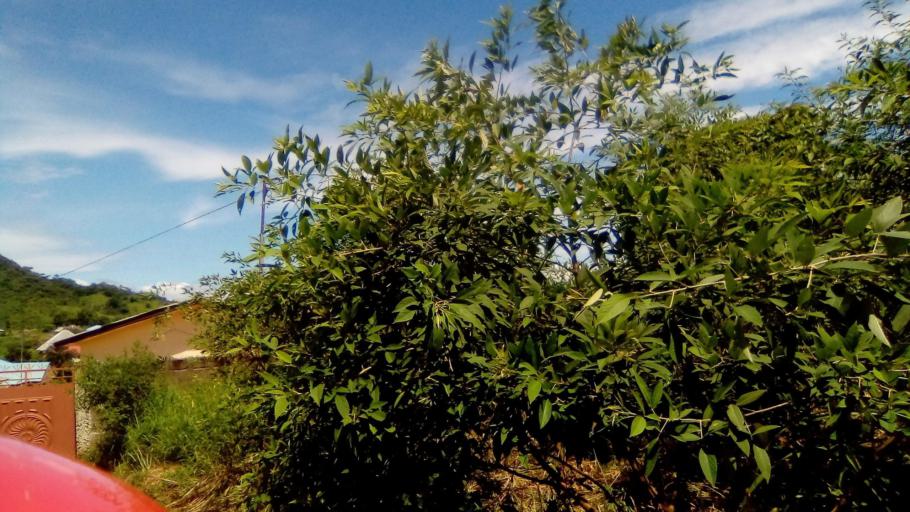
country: SL
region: Eastern Province
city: Simbakoro
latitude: 8.6328
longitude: -10.9966
